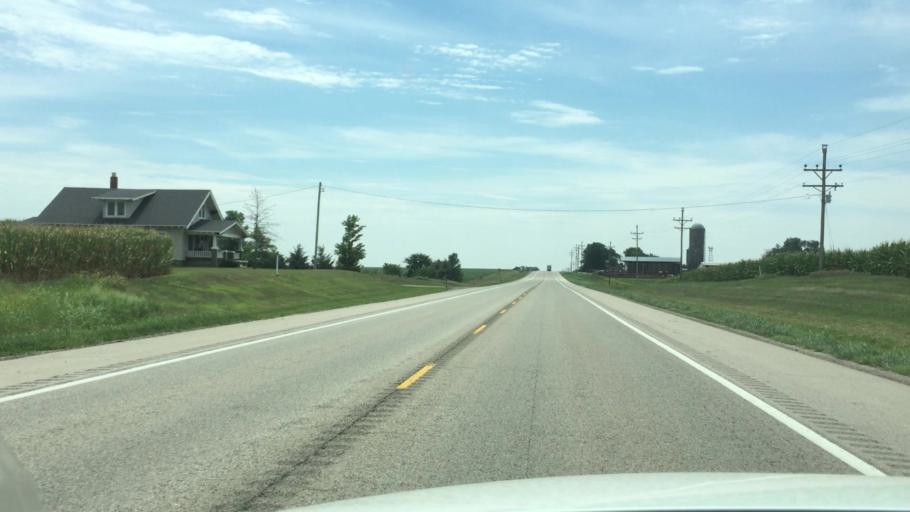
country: US
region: Kansas
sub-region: Nemaha County
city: Sabetha
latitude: 39.7773
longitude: -95.7295
